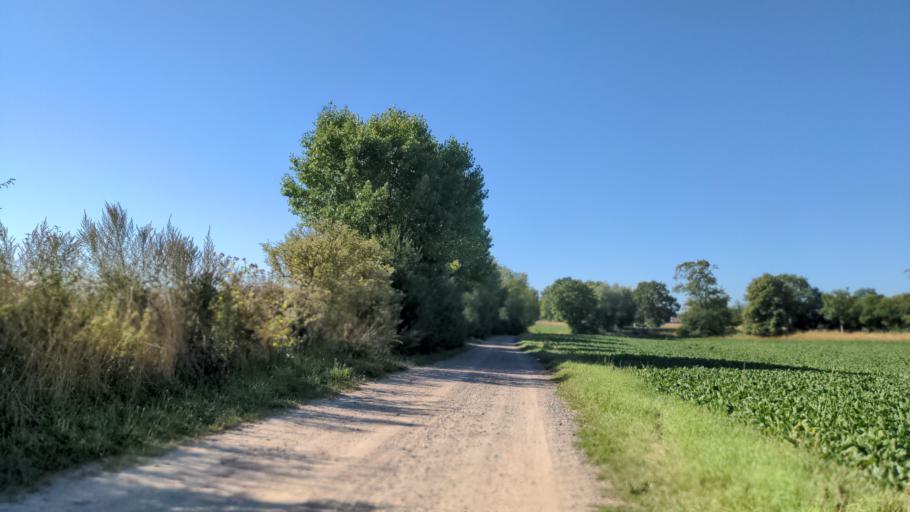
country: DE
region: Mecklenburg-Vorpommern
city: Ostseebad Boltenhagen
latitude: 53.9488
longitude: 11.2351
